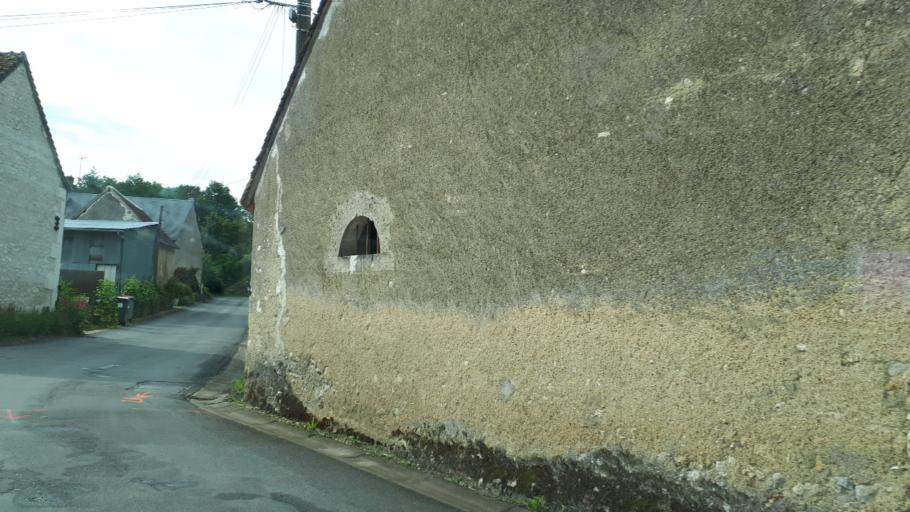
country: FR
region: Centre
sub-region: Departement du Loir-et-Cher
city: Villiers-sur-Loir
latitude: 47.7740
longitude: 1.0069
